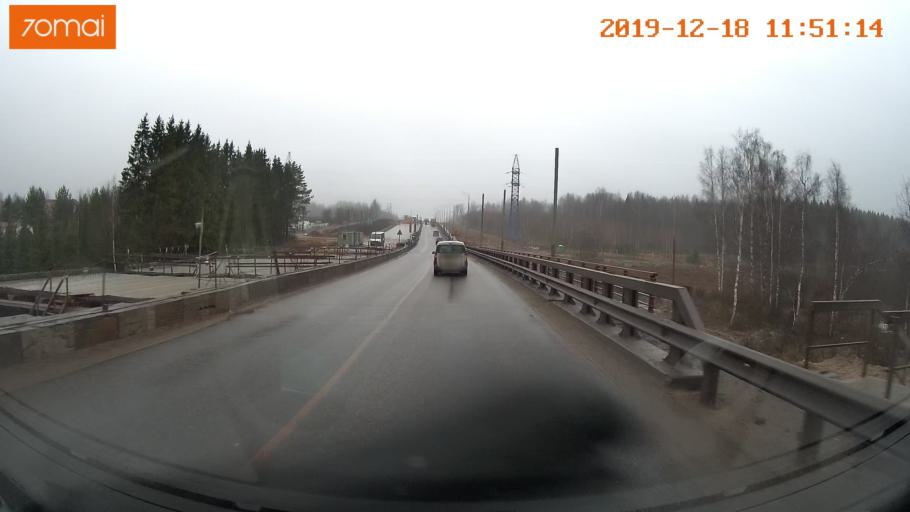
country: RU
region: Moskovskaya
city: Yershovo
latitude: 55.7919
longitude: 36.9219
